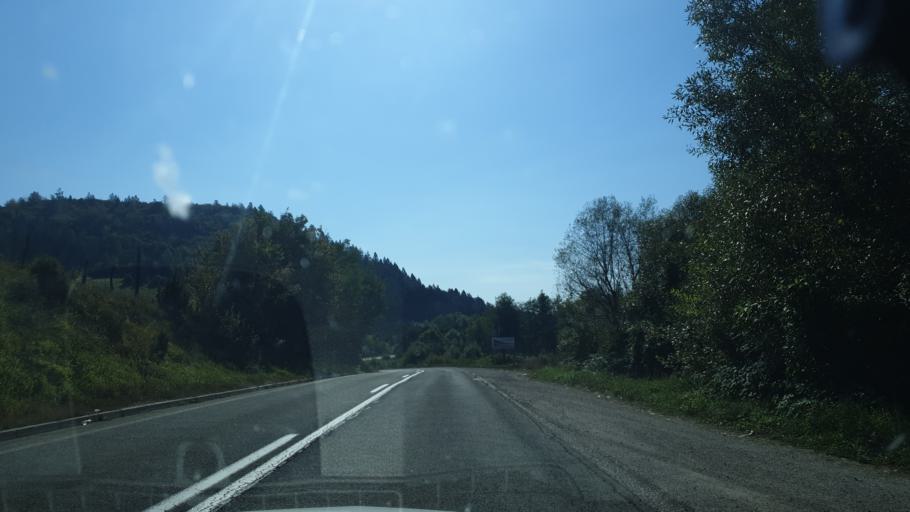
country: RS
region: Central Serbia
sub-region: Zlatiborski Okrug
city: Nova Varos
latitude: 43.5506
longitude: 19.7788
